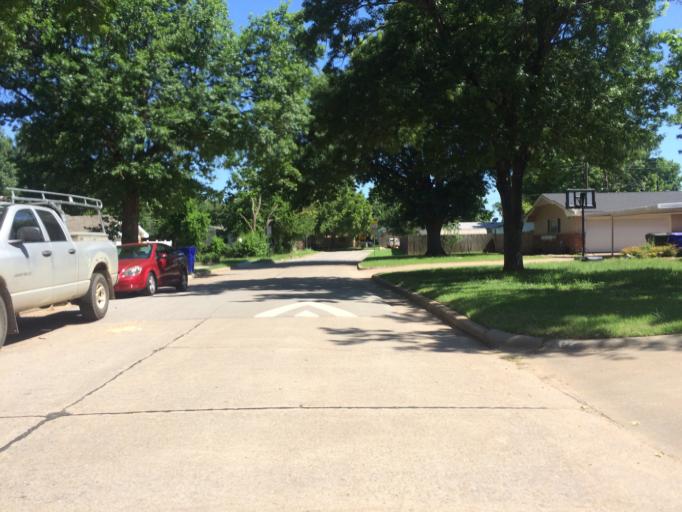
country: US
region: Oklahoma
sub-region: Cleveland County
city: Norman
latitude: 35.2234
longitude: -97.4673
